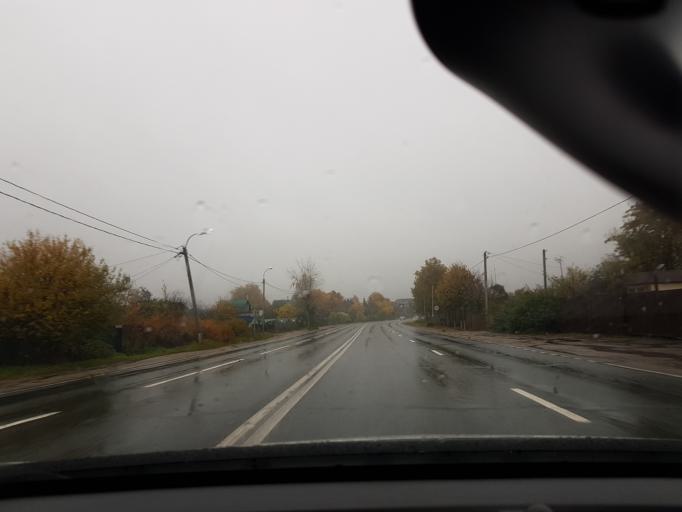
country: RU
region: Moskovskaya
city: Istra
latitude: 55.9066
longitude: 36.9346
